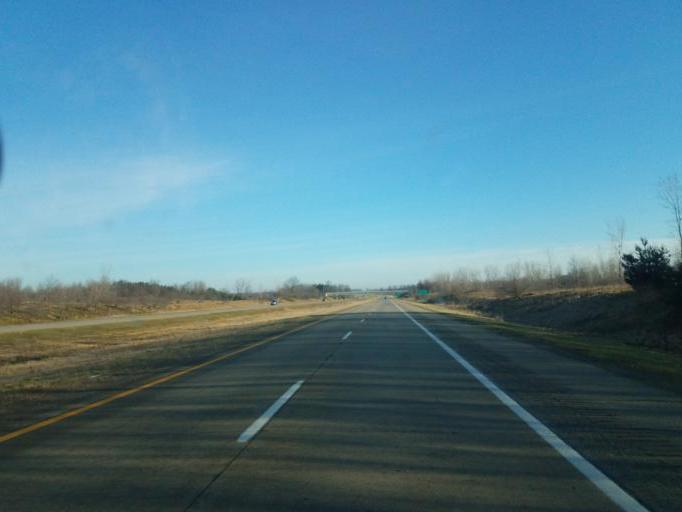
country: US
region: Michigan
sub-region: Clinton County
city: DeWitt
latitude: 42.9021
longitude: -84.5174
